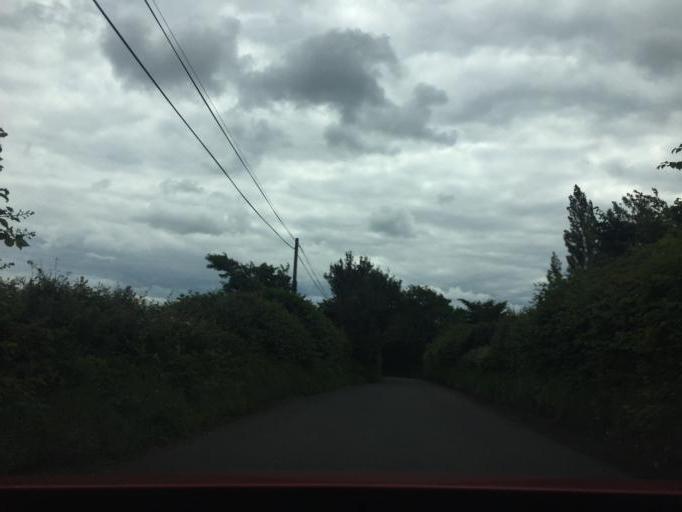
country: GB
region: England
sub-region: Hertfordshire
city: Wheathampstead
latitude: 51.8517
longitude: -0.3134
